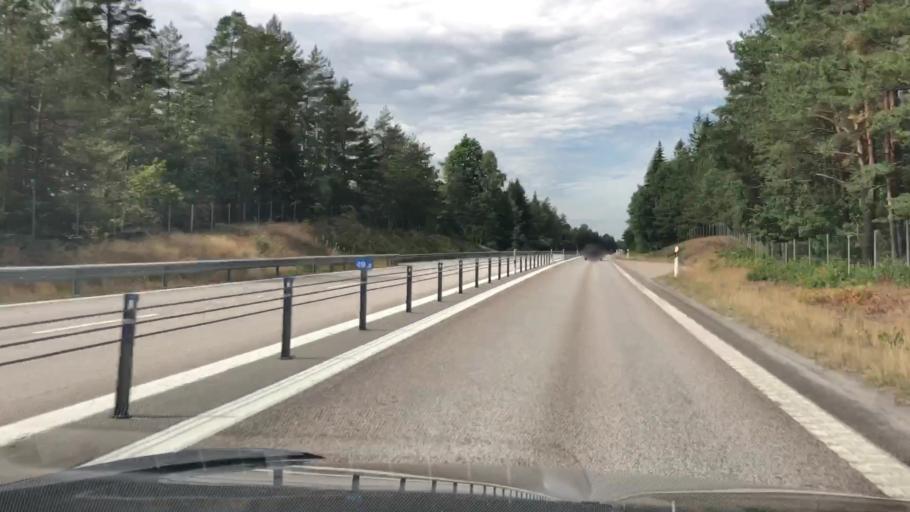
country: SE
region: Blekinge
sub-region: Ronneby Kommun
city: Brakne-Hoby
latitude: 56.2179
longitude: 15.1775
